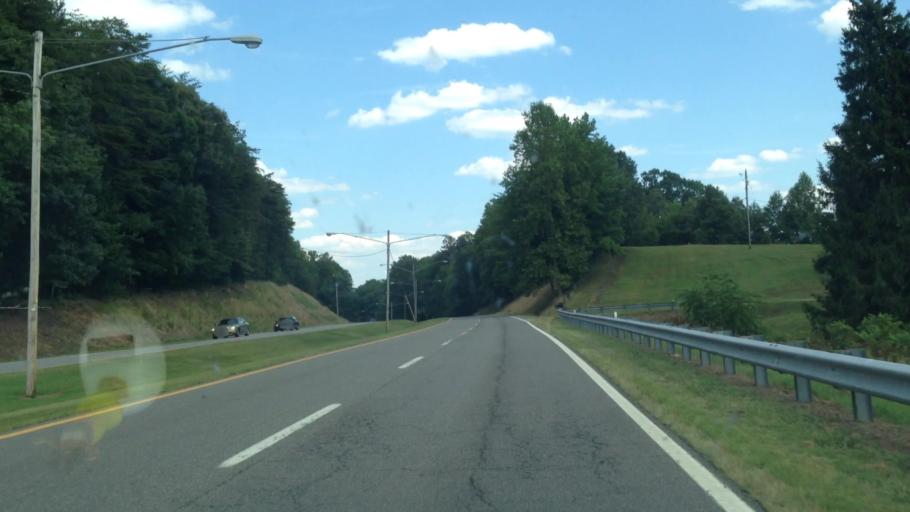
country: US
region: Virginia
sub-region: City of Danville
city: Danville
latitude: 36.5969
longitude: -79.5060
